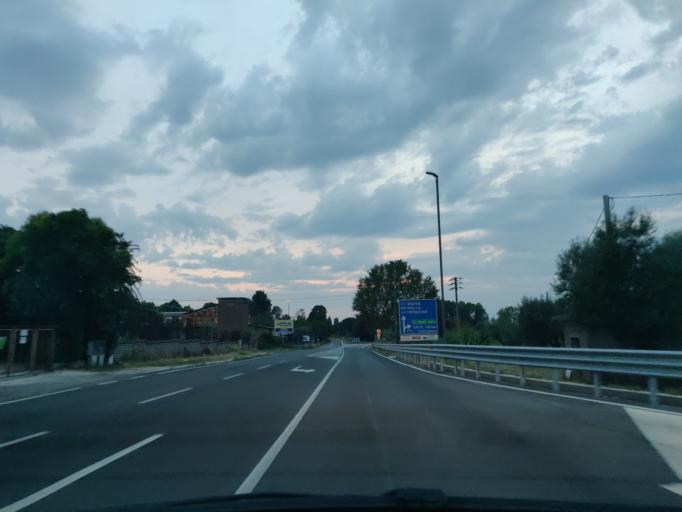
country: IT
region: Latium
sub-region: Provincia di Viterbo
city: Vetralla
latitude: 42.3727
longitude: 12.0619
